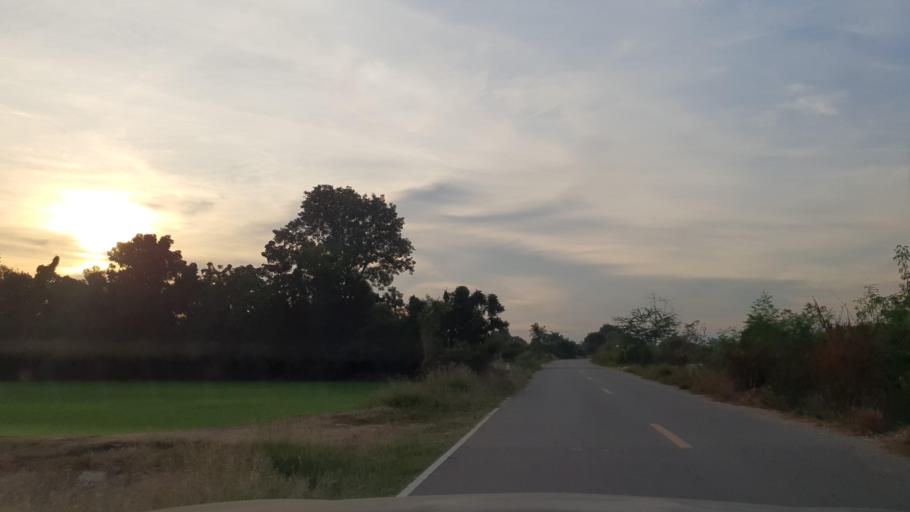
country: TH
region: Uthai Thani
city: Sawang Arom
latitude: 15.7152
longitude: 99.9558
